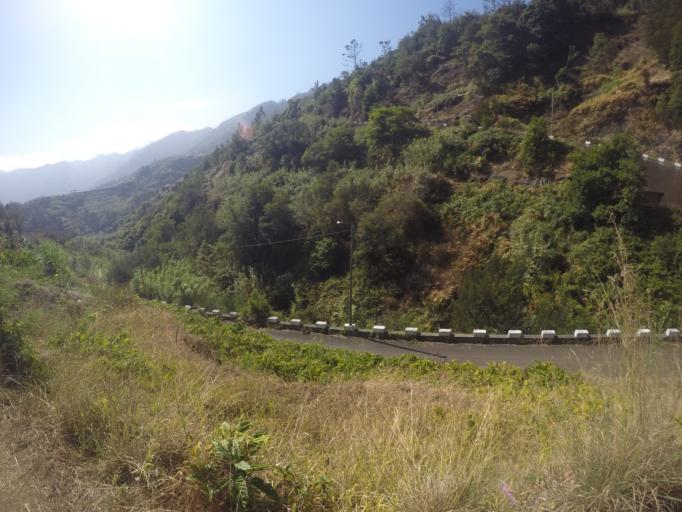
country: PT
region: Madeira
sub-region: Santana
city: Santana
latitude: 32.7576
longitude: -16.8341
